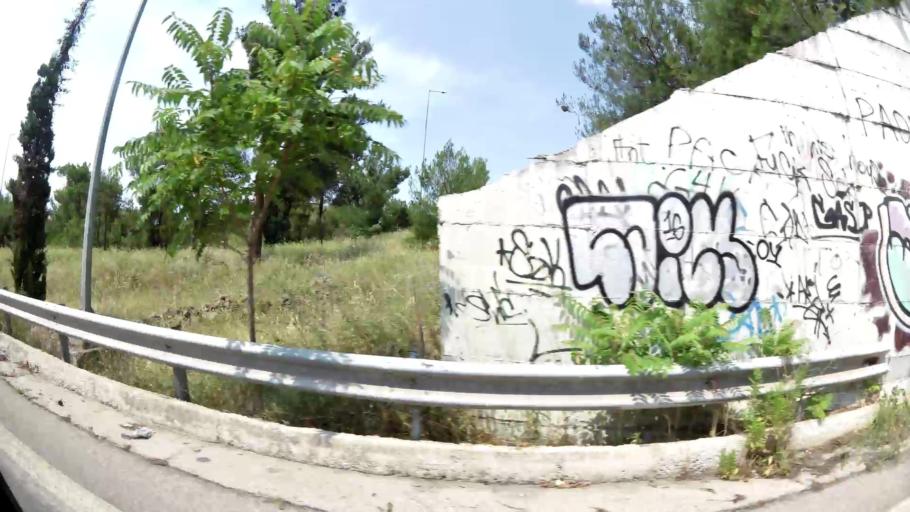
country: GR
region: Central Macedonia
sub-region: Nomos Thessalonikis
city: Agios Pavlos
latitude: 40.6341
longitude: 22.9717
